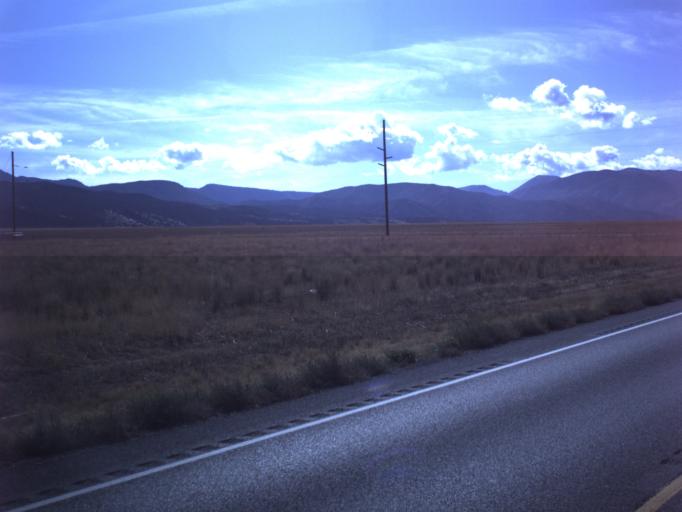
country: US
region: Utah
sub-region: Juab County
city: Nephi
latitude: 39.6324
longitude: -111.8617
